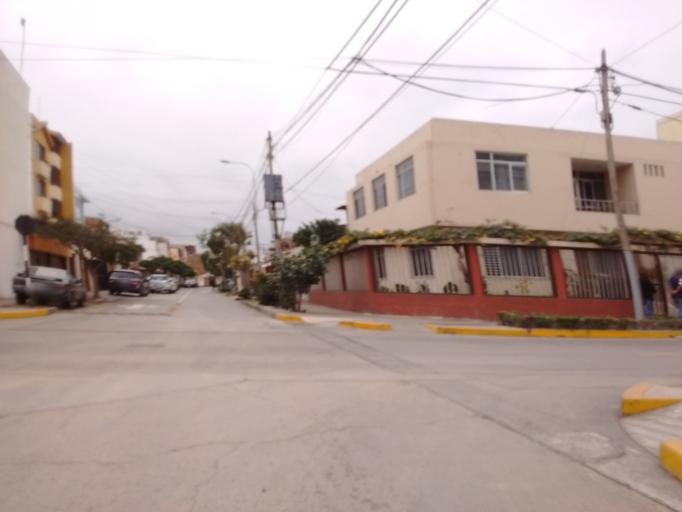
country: PE
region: Callao
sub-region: Callao
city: Callao
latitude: -12.0683
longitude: -77.0945
